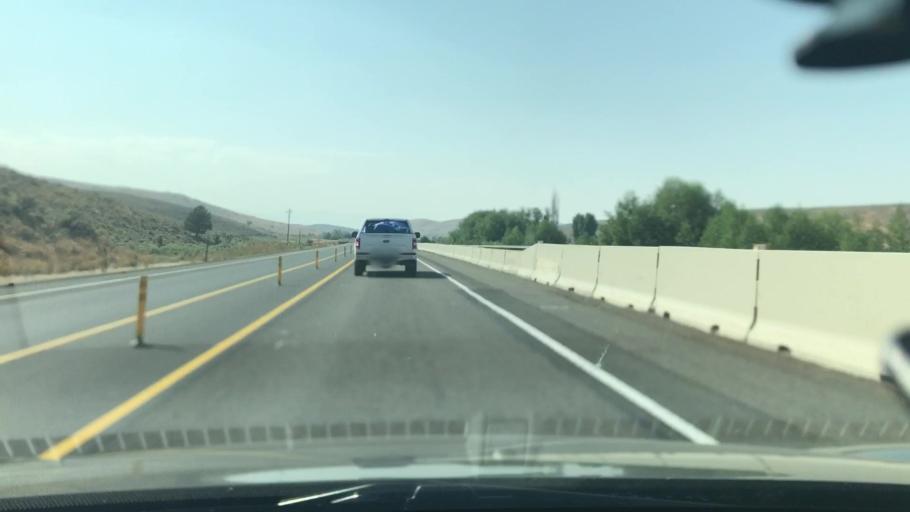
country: US
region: Oregon
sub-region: Baker County
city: Baker City
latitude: 44.6713
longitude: -117.6273
